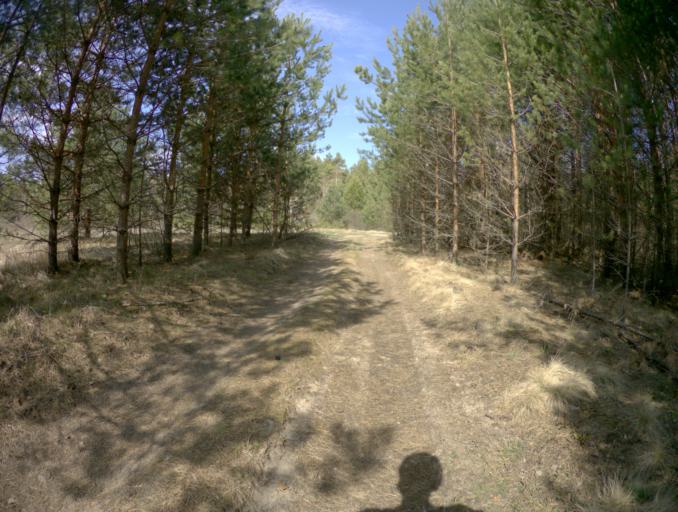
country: RU
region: Vladimir
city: Mezinovskiy
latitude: 55.5414
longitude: 40.2648
